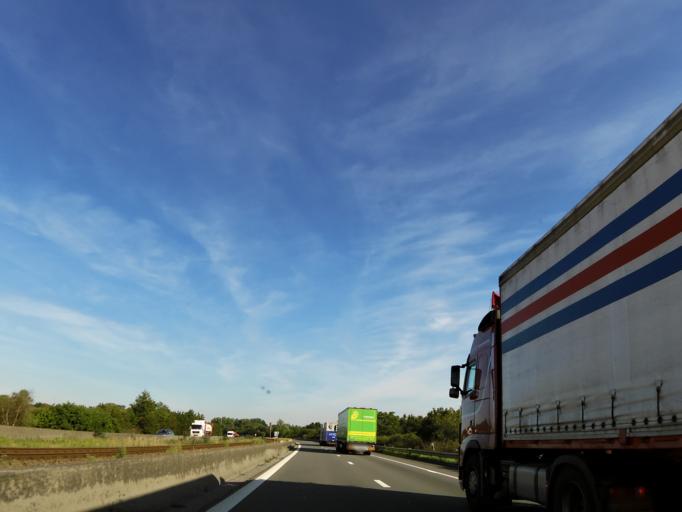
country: BE
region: Flanders
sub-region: Provincie Antwerpen
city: Stabroek
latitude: 51.3455
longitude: 4.3458
